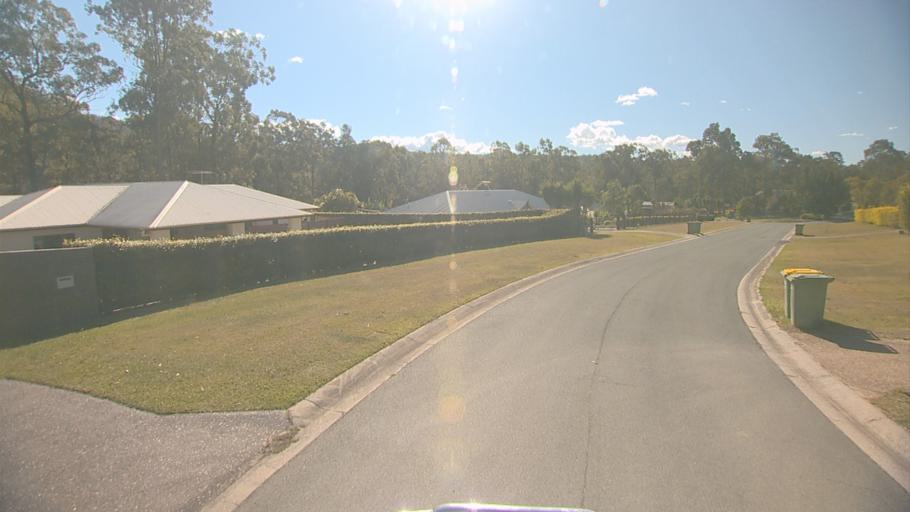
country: AU
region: Queensland
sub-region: Ipswich
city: Springfield Lakes
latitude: -27.7331
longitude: 152.9088
